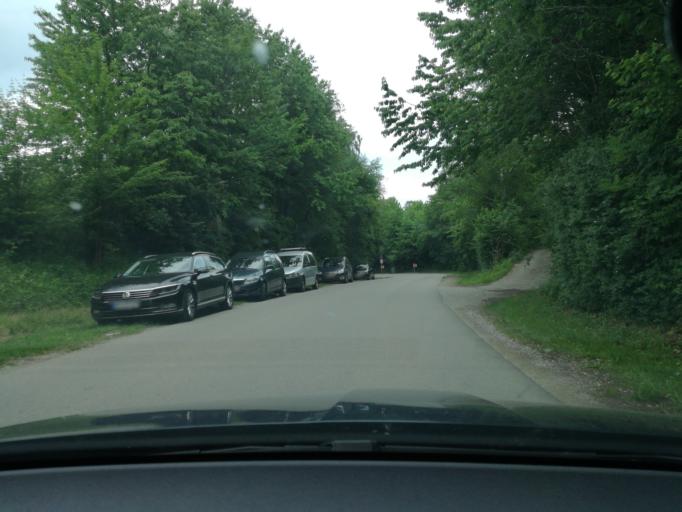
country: DE
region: Bavaria
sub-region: Upper Bavaria
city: Utting am Ammersee
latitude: 48.0328
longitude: 11.0945
